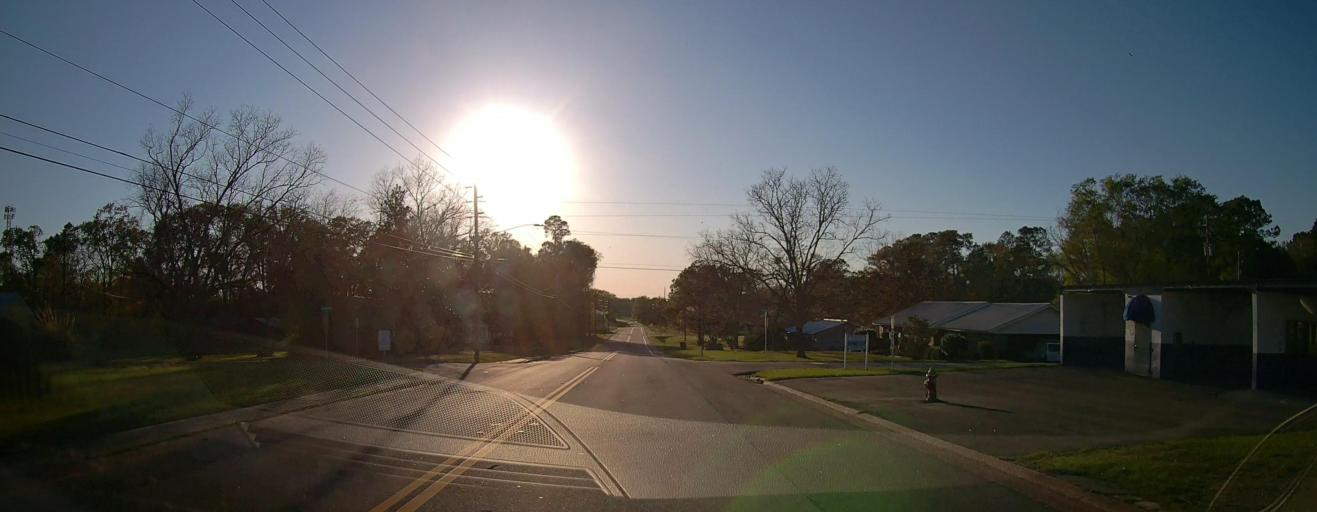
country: US
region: Georgia
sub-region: Wilcox County
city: Abbeville
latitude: 31.9924
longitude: -83.3090
